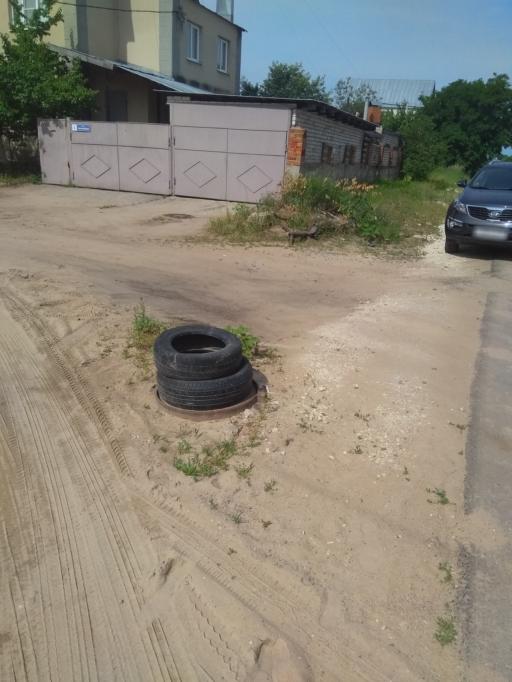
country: RU
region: Voronezj
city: Pridonskoy
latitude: 51.6447
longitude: 39.0909
